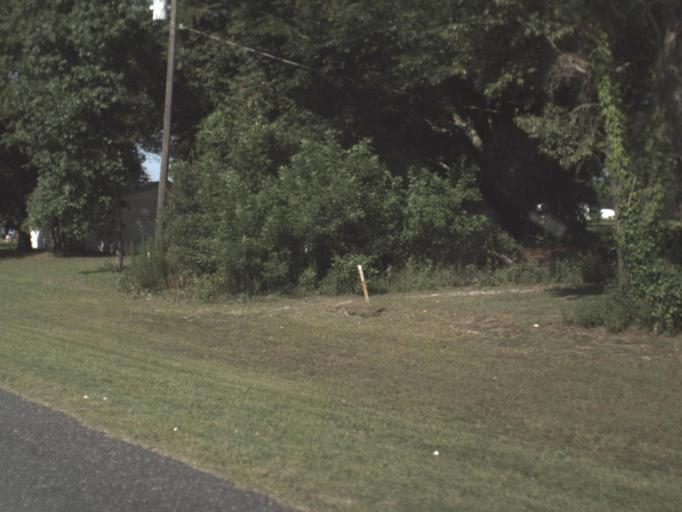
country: US
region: Florida
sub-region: Columbia County
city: Lake City
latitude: 30.0441
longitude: -82.7056
